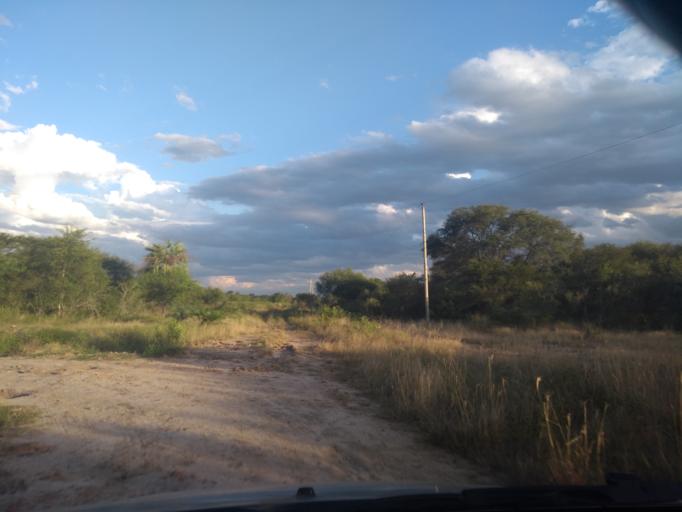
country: AR
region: Chaco
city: Colonia Benitez
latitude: -27.3907
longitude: -58.9434
